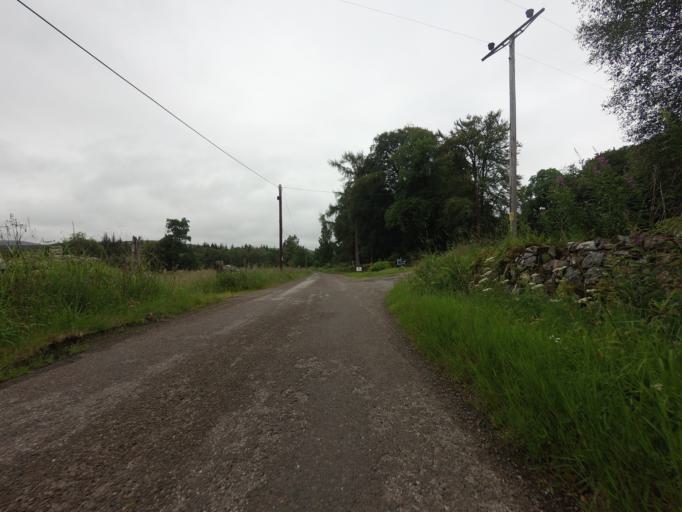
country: GB
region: Scotland
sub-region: Highland
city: Evanton
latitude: 57.9830
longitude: -4.4188
